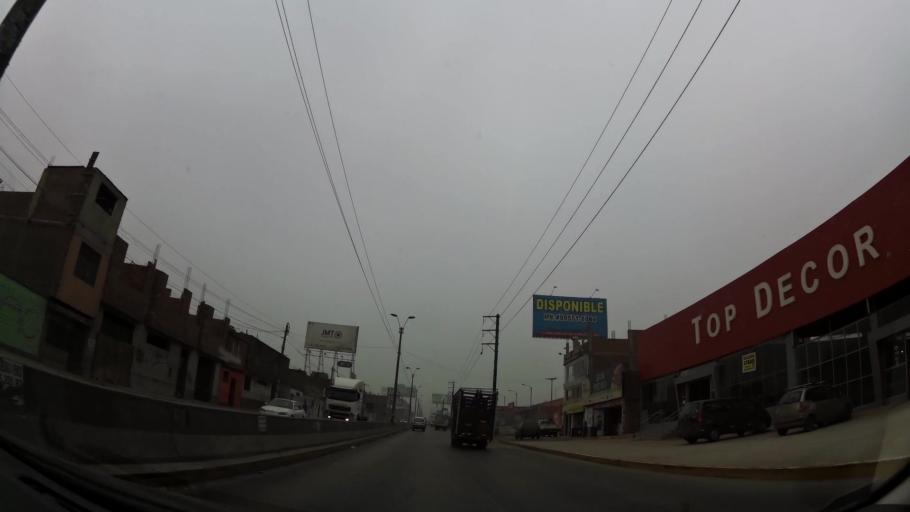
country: PE
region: Lima
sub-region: Lima
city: Santa Maria
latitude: -12.0157
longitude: -76.8885
